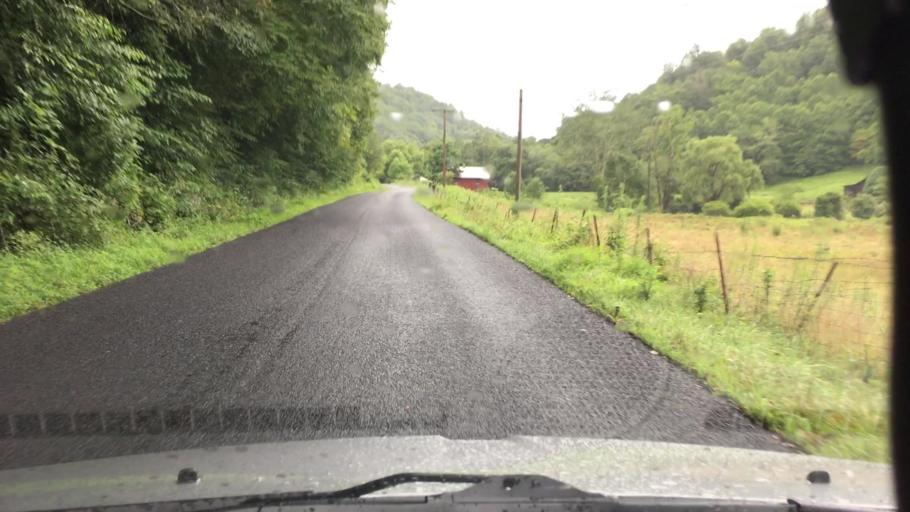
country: US
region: North Carolina
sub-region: Madison County
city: Mars Hill
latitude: 35.9123
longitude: -82.5071
